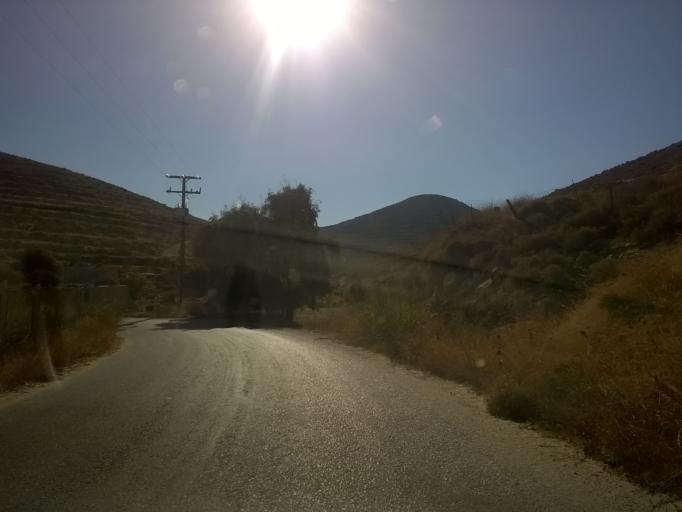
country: GR
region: South Aegean
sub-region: Nomos Kykladon
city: Naxos
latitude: 37.1262
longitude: 25.4390
